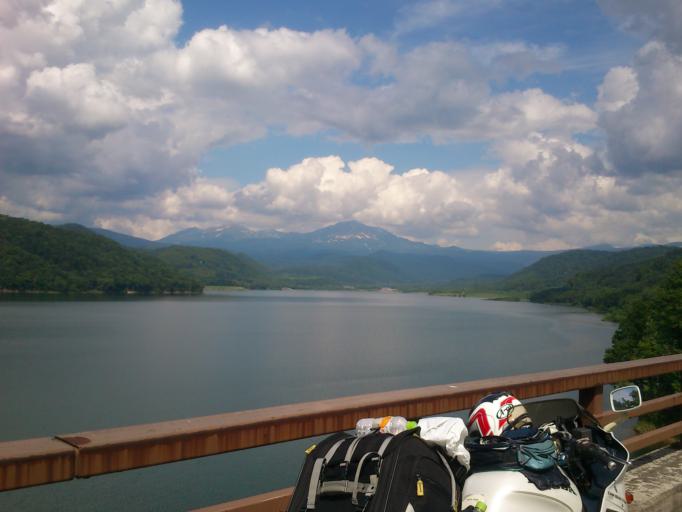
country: JP
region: Hokkaido
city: Kamikawa
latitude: 43.6212
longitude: 142.6331
